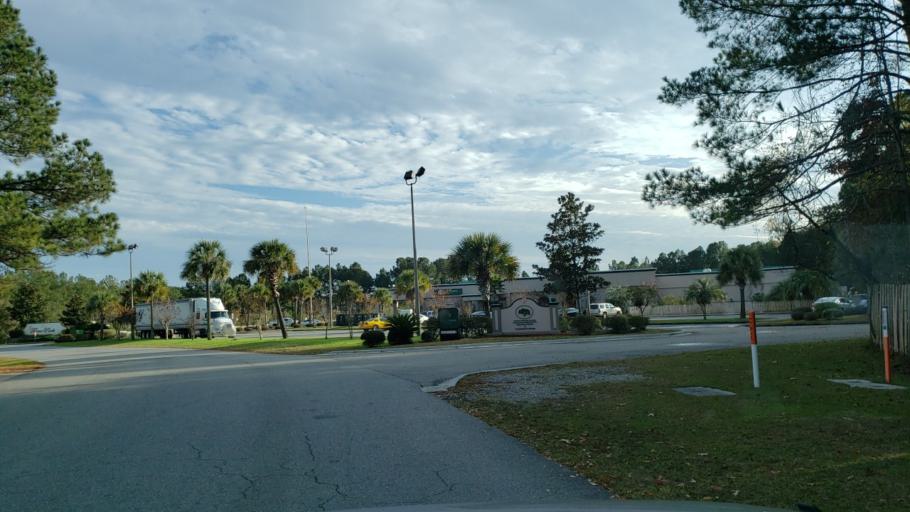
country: US
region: Georgia
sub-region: Chatham County
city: Pooler
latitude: 32.1108
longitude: -81.2402
